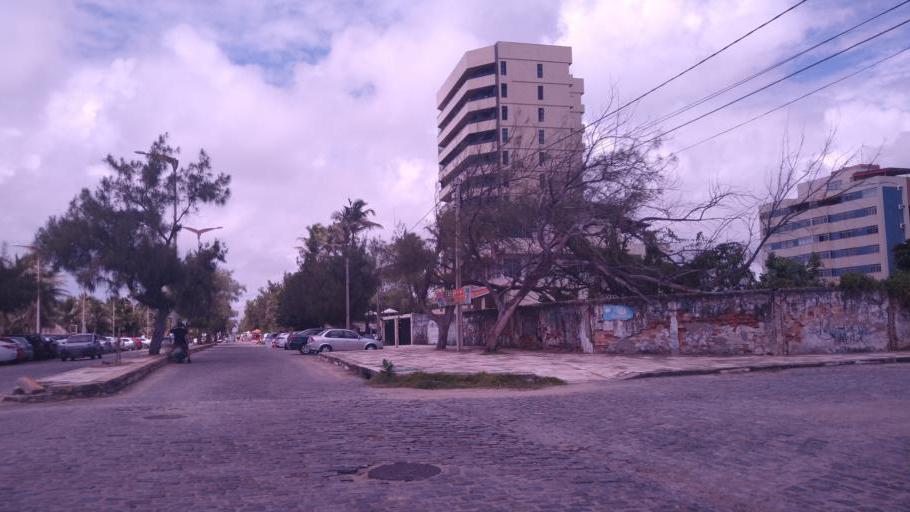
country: BR
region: Ceara
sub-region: Fortaleza
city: Fortaleza
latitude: -3.7319
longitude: -38.4574
